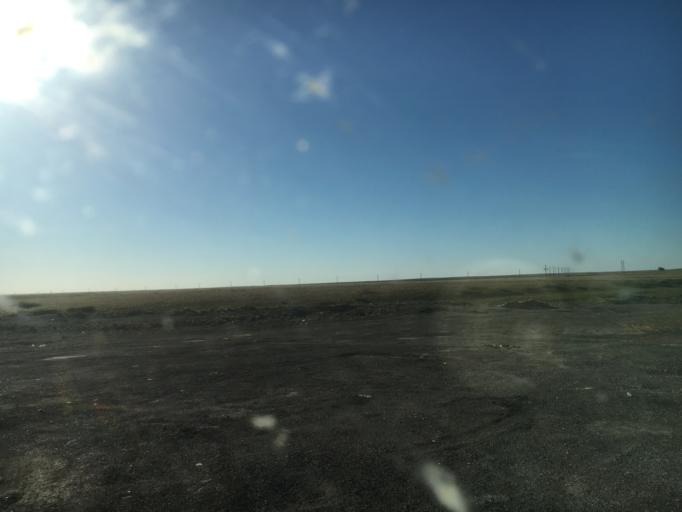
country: KZ
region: Aqtoebe
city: Khromtau
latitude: 50.2529
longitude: 58.3703
